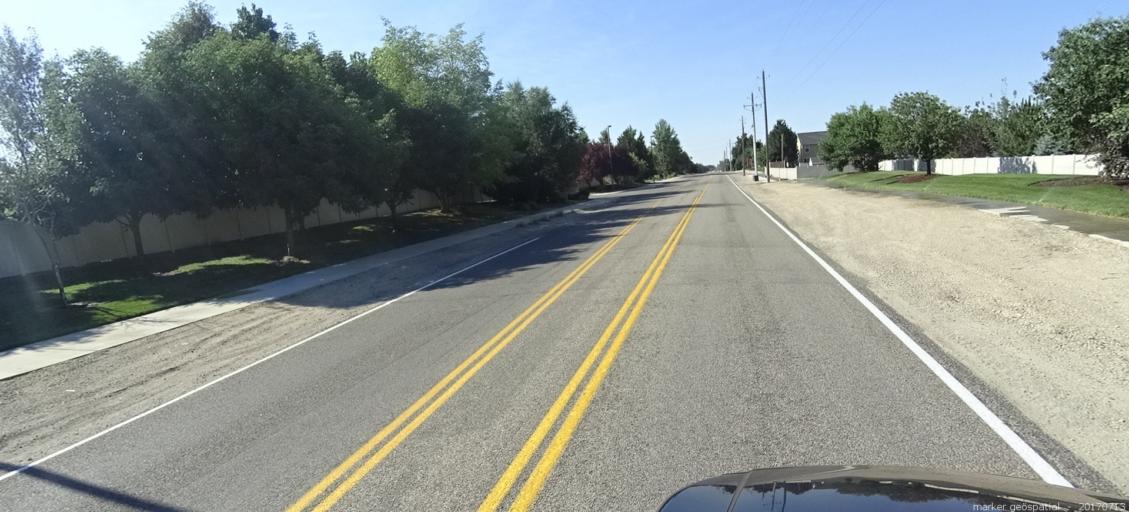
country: US
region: Idaho
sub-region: Ada County
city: Kuna
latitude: 43.5150
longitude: -116.4139
